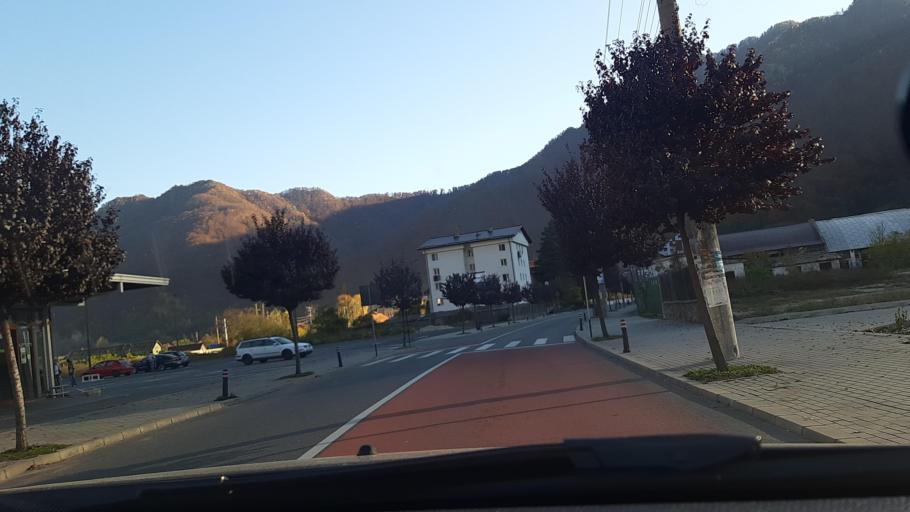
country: RO
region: Valcea
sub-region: Comuna Brezoi
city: Brezoi
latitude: 45.3407
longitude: 24.2472
